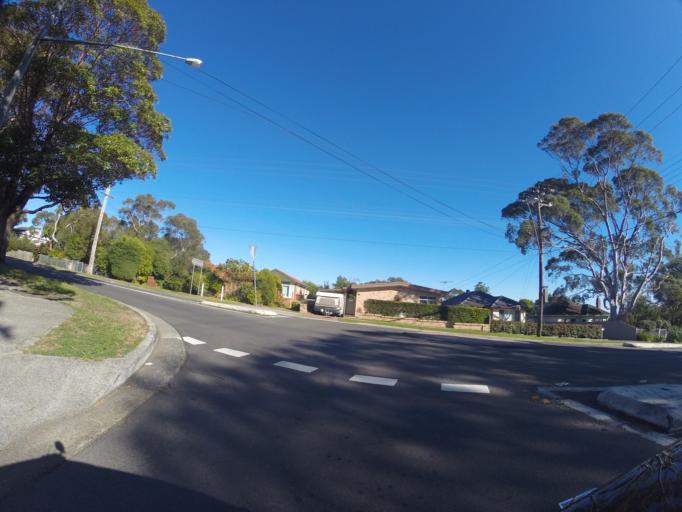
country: AU
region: New South Wales
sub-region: Sutherland Shire
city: Engadine
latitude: -34.0564
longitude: 151.0037
